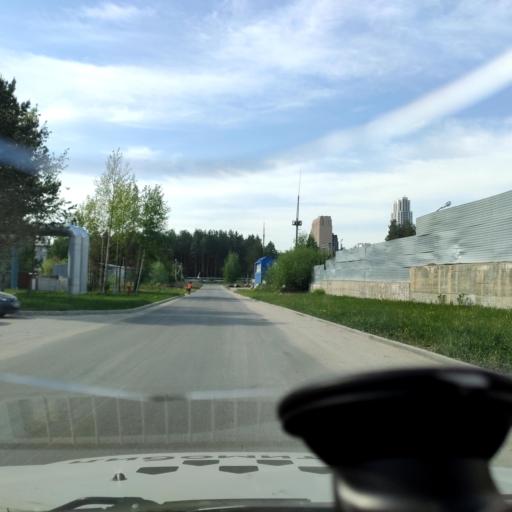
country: RU
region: Sverdlovsk
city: Sovkhoznyy
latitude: 56.7732
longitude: 60.5555
